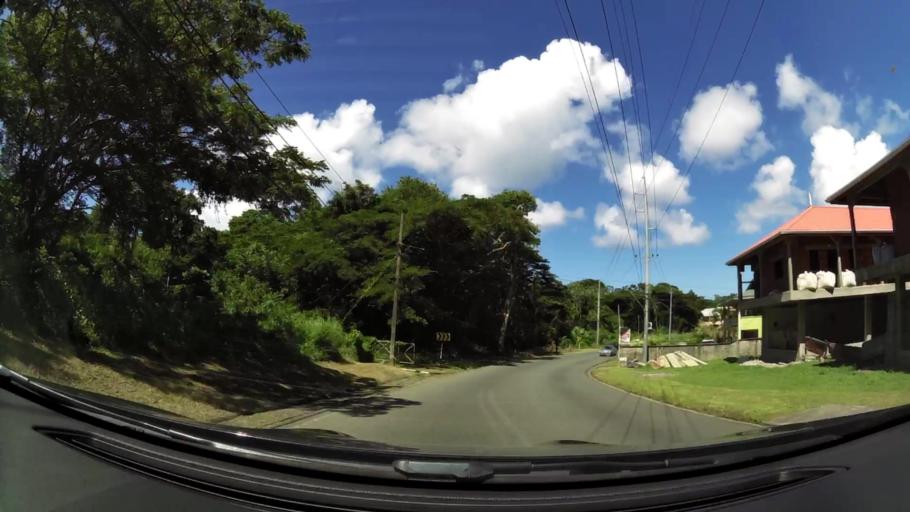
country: TT
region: Tobago
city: Scarborough
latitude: 11.1747
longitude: -60.8017
